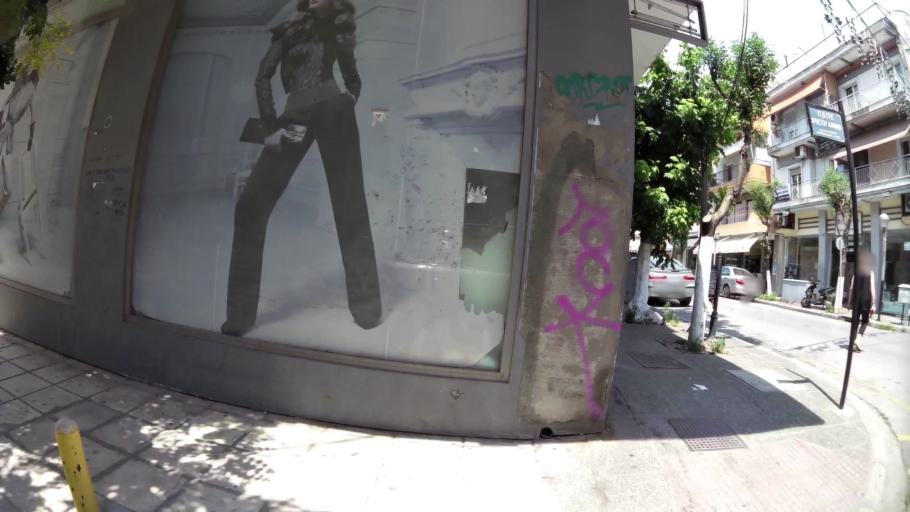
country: GR
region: Central Macedonia
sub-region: Nomos Thessalonikis
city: Ampelokipoi
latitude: 40.6504
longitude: 22.9225
